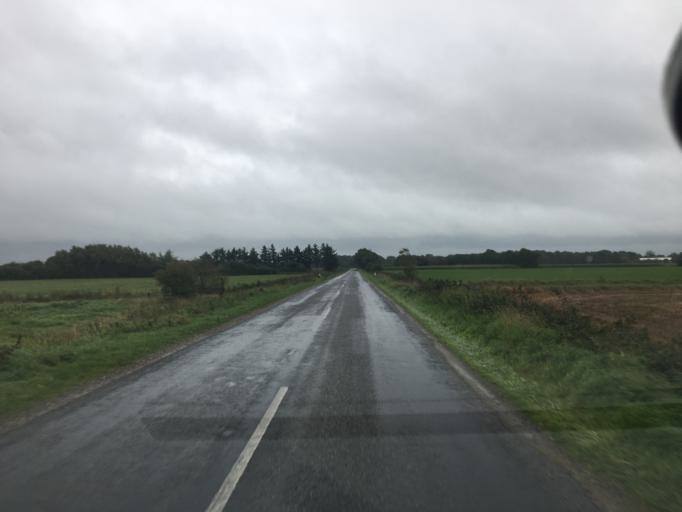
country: DE
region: Schleswig-Holstein
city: Bramstedtlund
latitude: 54.9661
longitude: 9.0478
